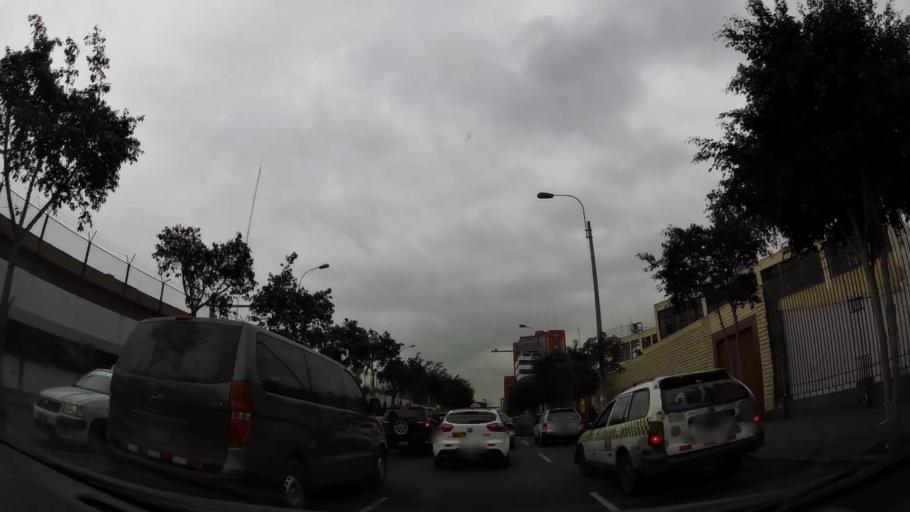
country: PE
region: Lima
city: Lima
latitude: -12.0564
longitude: -77.0273
